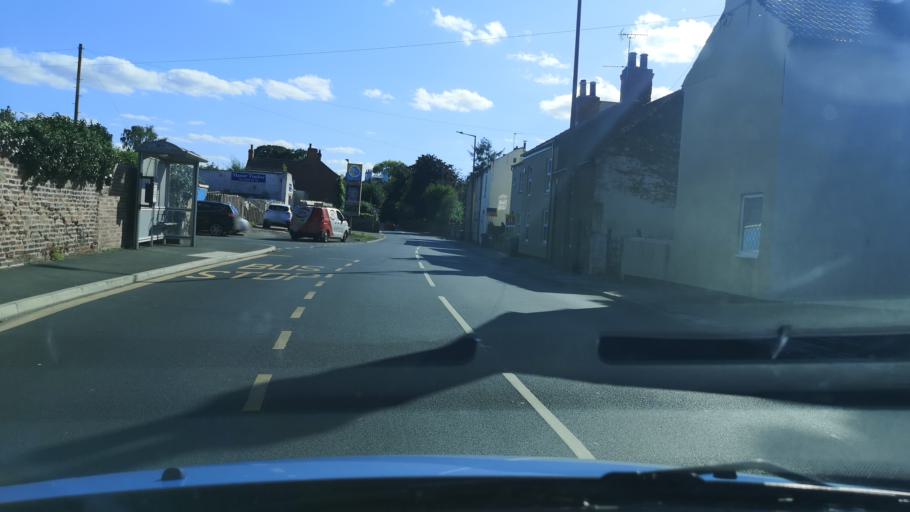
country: GB
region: England
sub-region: Doncaster
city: Hatfield
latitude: 53.5760
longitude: -1.0012
